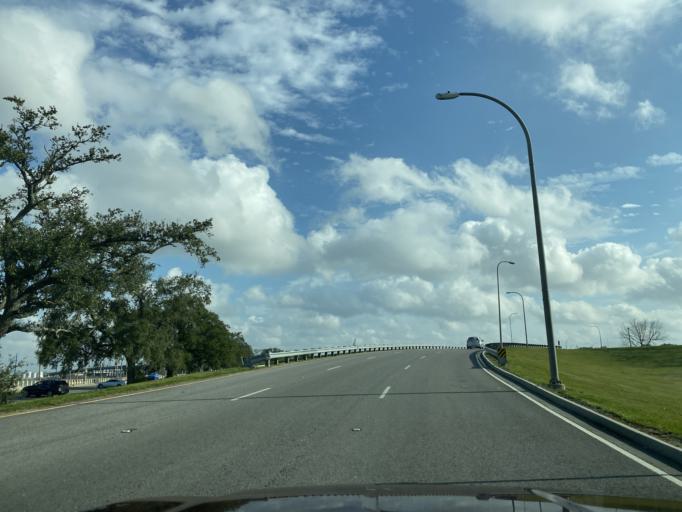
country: US
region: Louisiana
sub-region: Orleans Parish
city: New Orleans
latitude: 30.0346
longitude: -90.0422
